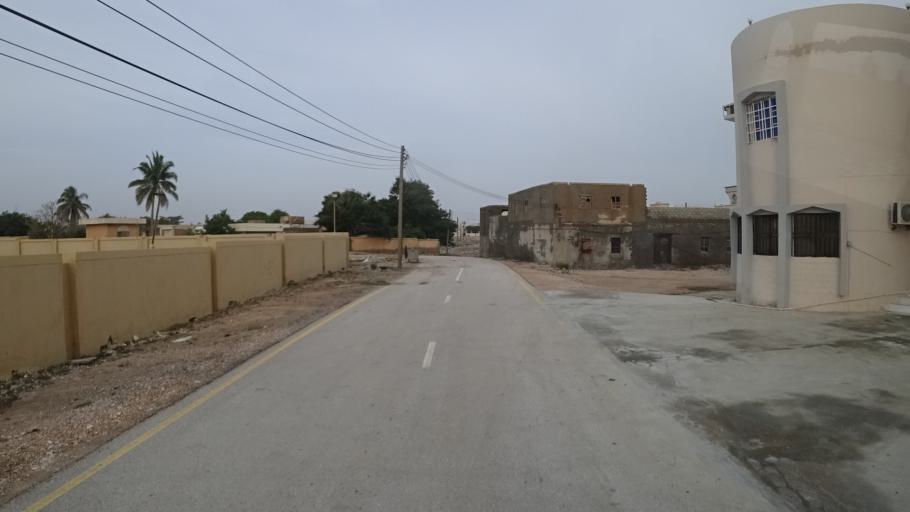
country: OM
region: Zufar
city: Salalah
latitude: 16.9905
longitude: 54.6946
